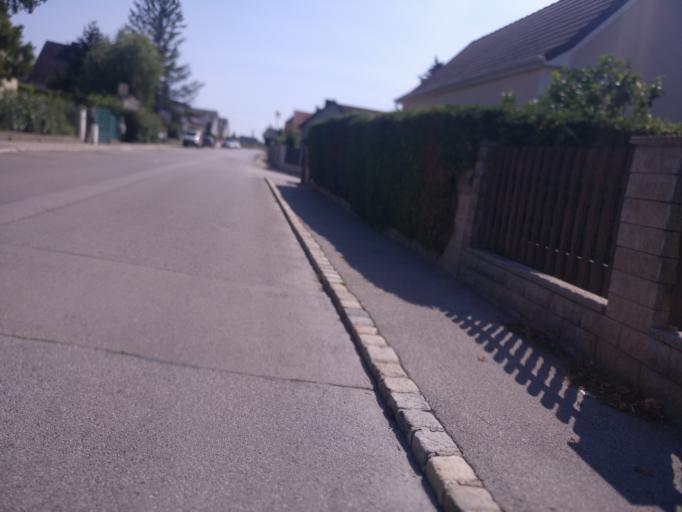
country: AT
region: Lower Austria
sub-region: Politischer Bezirk Modling
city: Guntramsdorf
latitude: 48.0401
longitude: 16.3110
